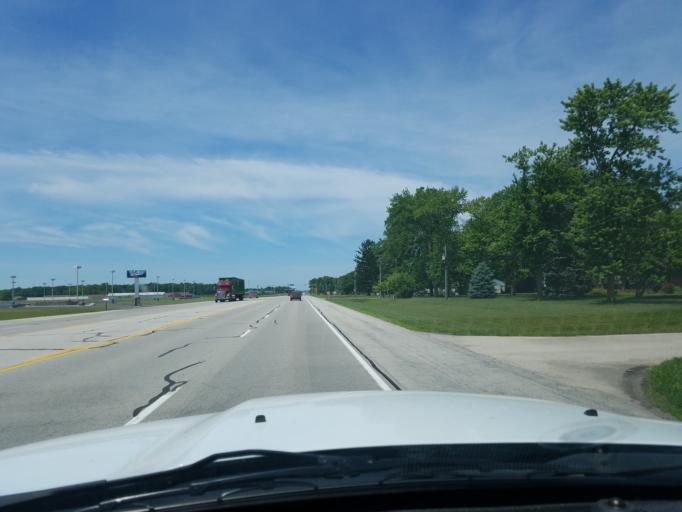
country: US
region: Indiana
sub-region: Delaware County
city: Daleville
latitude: 40.1134
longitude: -85.5307
